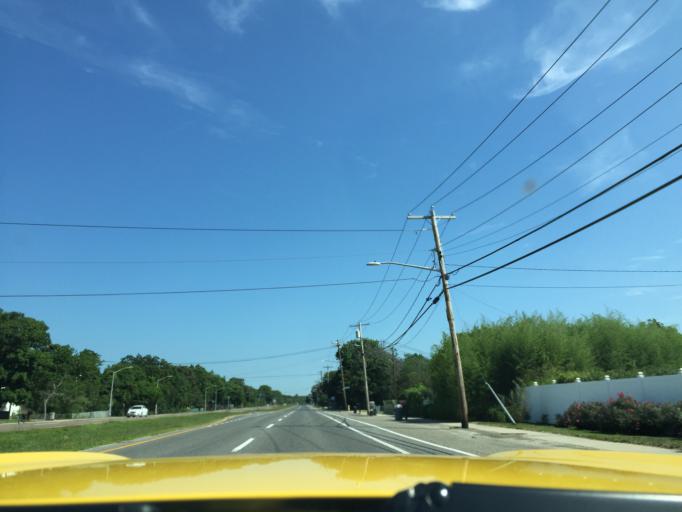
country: US
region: New York
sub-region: Suffolk County
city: Mastic Beach
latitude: 40.7472
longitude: -72.8714
